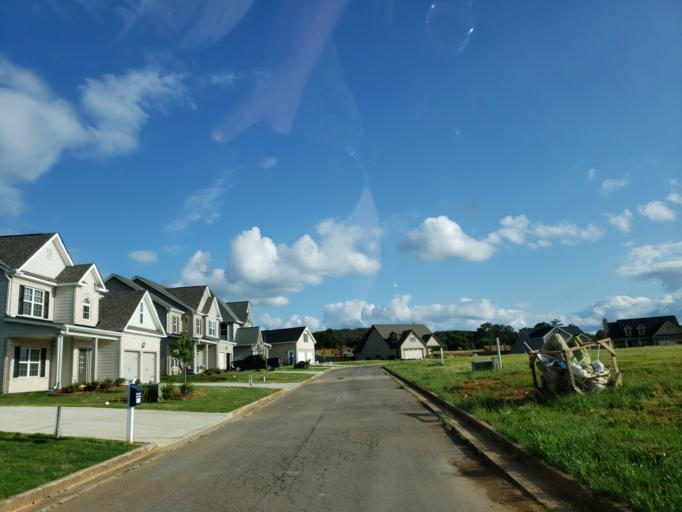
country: US
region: Georgia
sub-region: Bartow County
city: Adairsville
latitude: 34.3898
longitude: -84.8954
